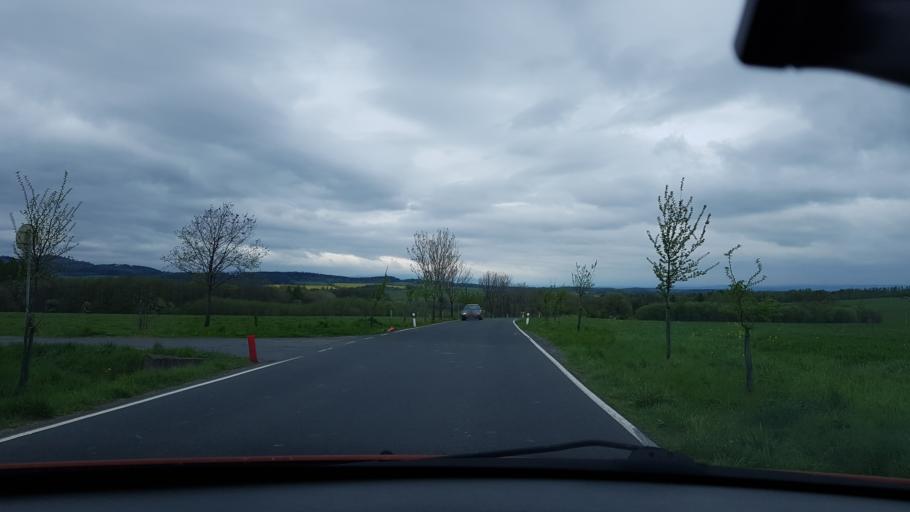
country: CZ
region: Olomoucky
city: Mikulovice
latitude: 50.3104
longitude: 17.3022
